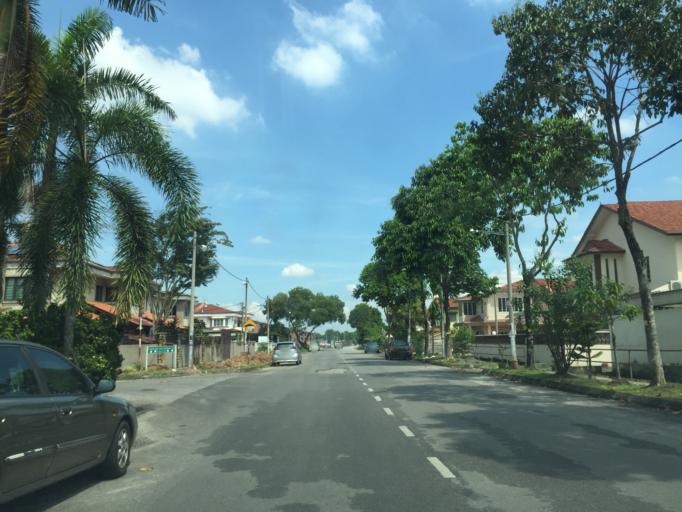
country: MY
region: Selangor
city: Klang
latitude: 3.0050
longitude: 101.4712
